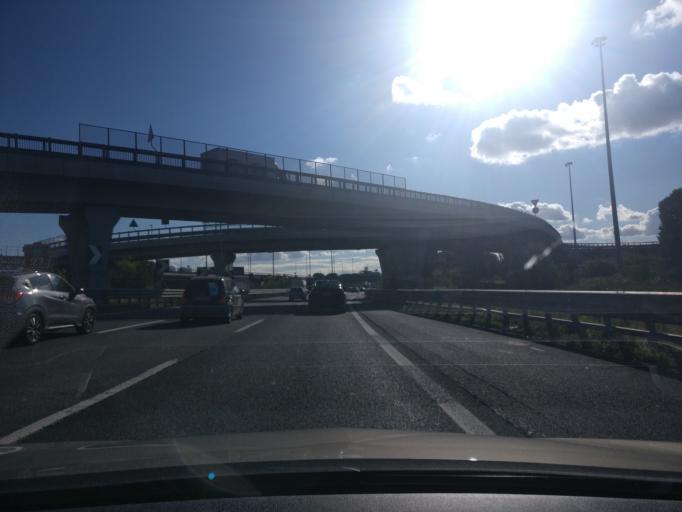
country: IT
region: Latium
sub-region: Citta metropolitana di Roma Capitale
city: Ciampino
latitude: 41.8240
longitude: 12.5807
